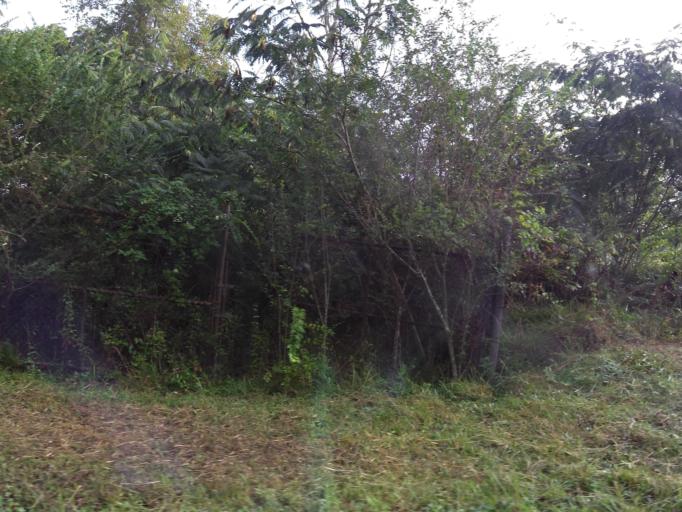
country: US
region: Tennessee
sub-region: Campbell County
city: Jellico
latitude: 36.5857
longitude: -84.1256
